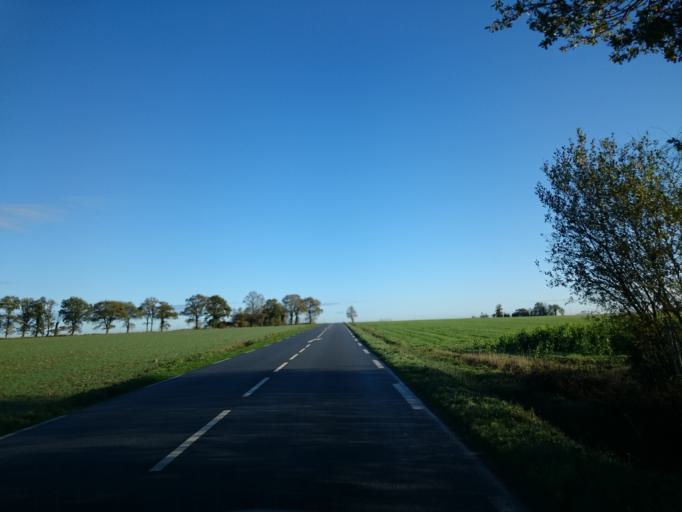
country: FR
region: Brittany
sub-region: Departement d'Ille-et-Vilaine
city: Tresboeuf
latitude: 47.9325
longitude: -1.5435
